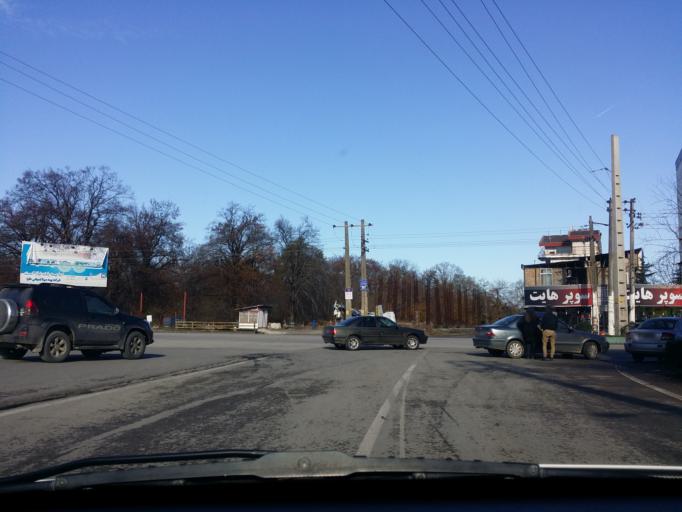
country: IR
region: Mazandaran
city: Chalus
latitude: 36.6875
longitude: 51.3125
